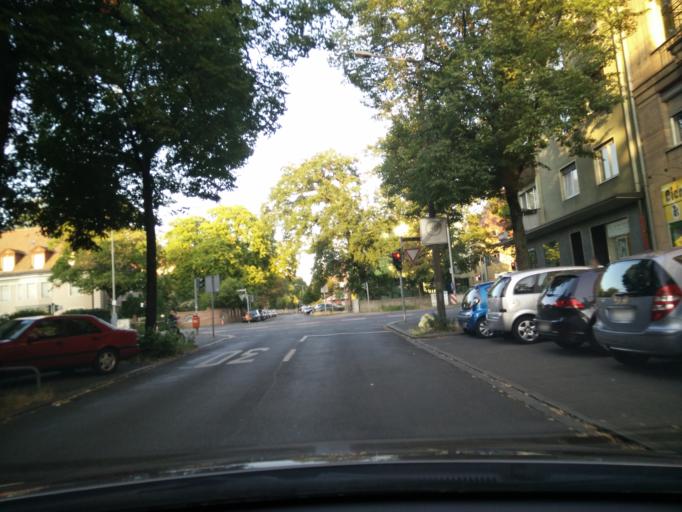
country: DE
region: Bavaria
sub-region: Regierungsbezirk Mittelfranken
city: Nuernberg
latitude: 49.4318
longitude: 11.0860
